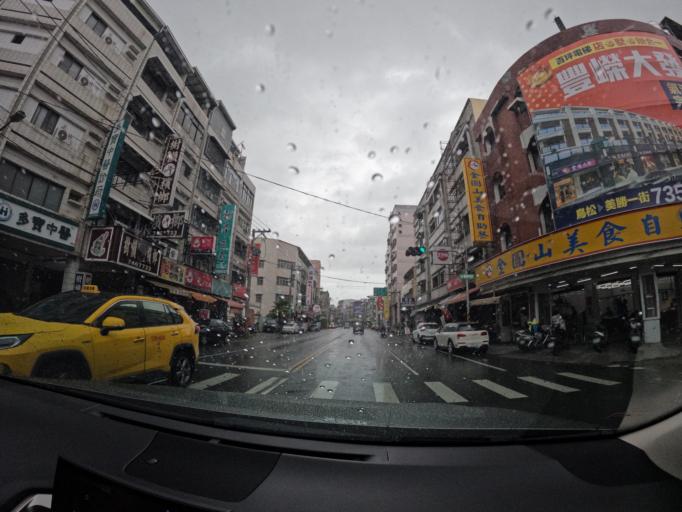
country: TW
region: Taiwan
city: Fengshan
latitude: 22.6376
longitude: 120.3644
